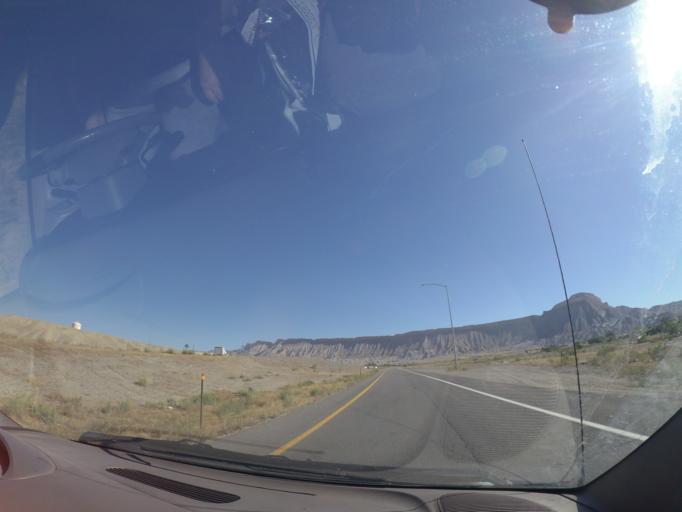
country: US
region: Colorado
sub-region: Mesa County
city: Clifton
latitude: 39.1016
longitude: -108.4472
